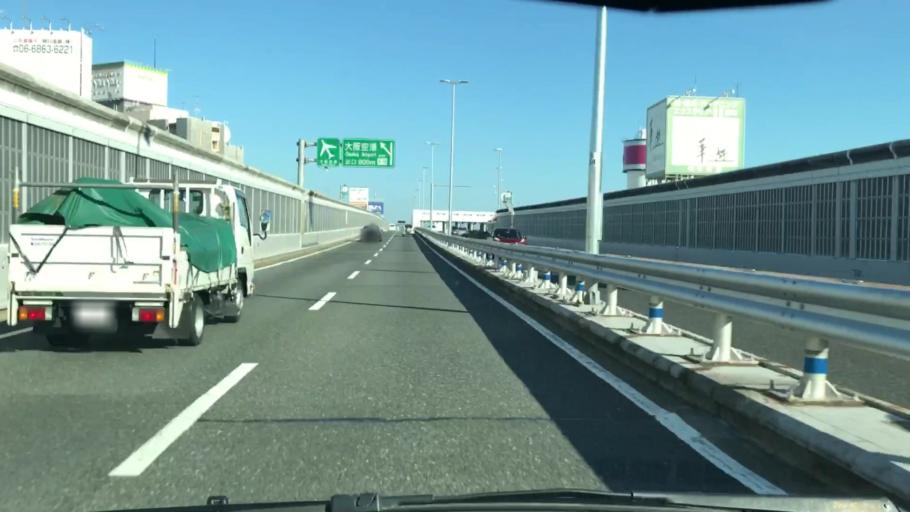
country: JP
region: Osaka
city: Toyonaka
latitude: 34.7817
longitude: 135.4537
